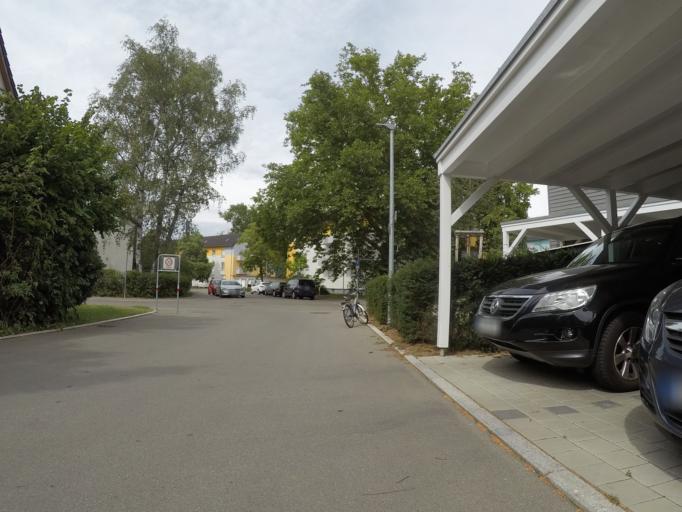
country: DE
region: Baden-Wuerttemberg
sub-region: Tuebingen Region
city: Pfullingen
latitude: 48.4874
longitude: 9.2280
